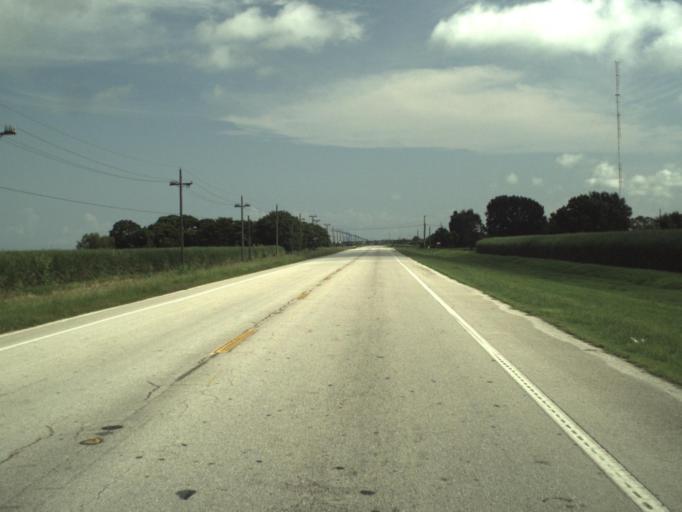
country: US
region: Florida
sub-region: Palm Beach County
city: Belle Glade
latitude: 26.7082
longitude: -80.6840
